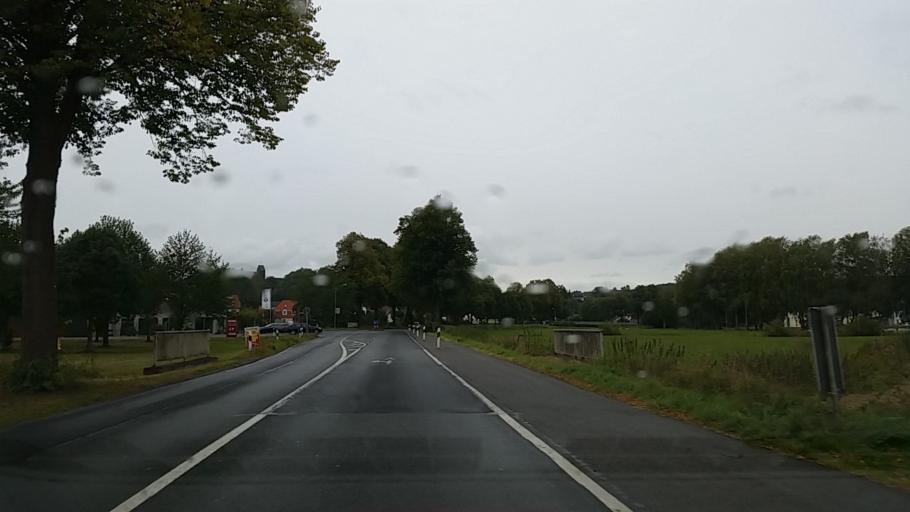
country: DE
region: Lower Saxony
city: Katlenburg-Lindau
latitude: 51.6819
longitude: 10.1087
